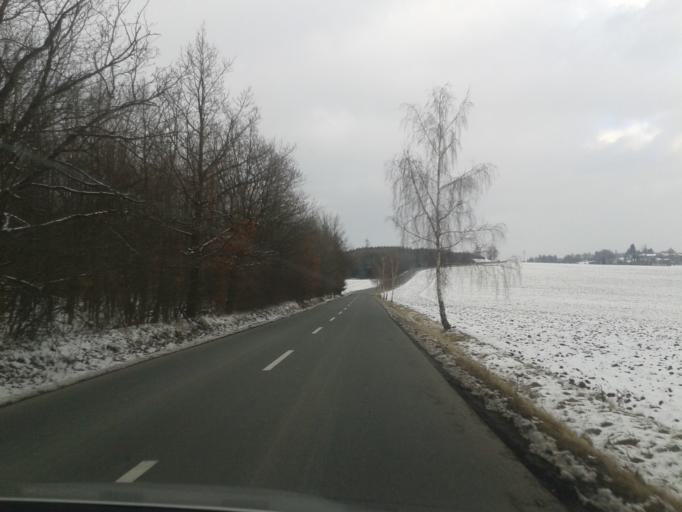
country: CZ
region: Olomoucky
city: Konice
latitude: 49.5983
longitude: 16.8891
